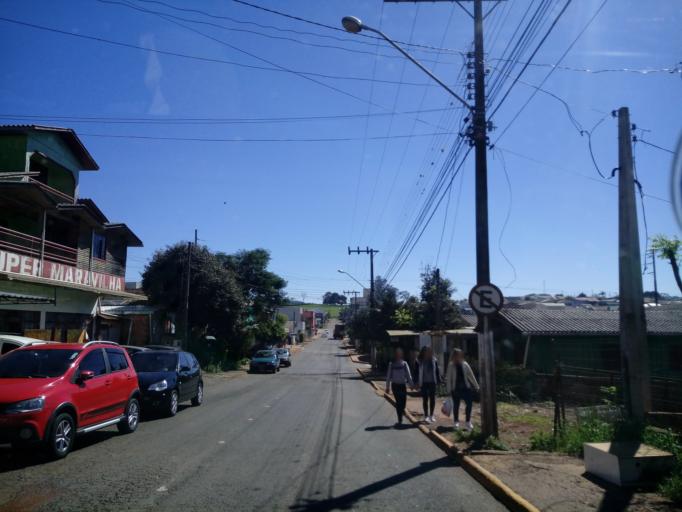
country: BR
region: Santa Catarina
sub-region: Chapeco
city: Chapeco
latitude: -27.0917
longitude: -52.6740
